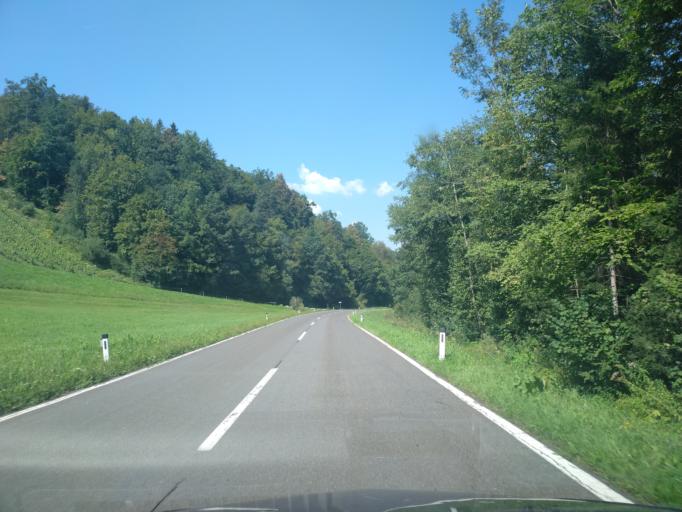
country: AT
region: Styria
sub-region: Politischer Bezirk Leibnitz
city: Gamlitz
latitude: 46.7096
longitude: 15.5065
